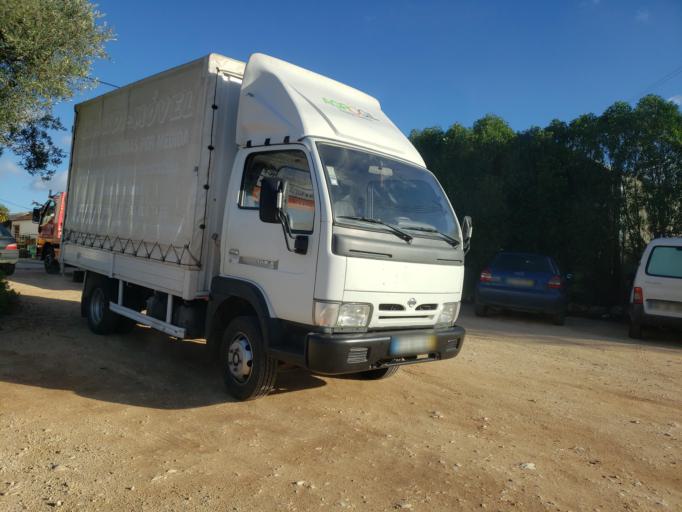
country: PT
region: Faro
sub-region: Portimao
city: Alvor
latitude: 37.1934
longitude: -8.5898
